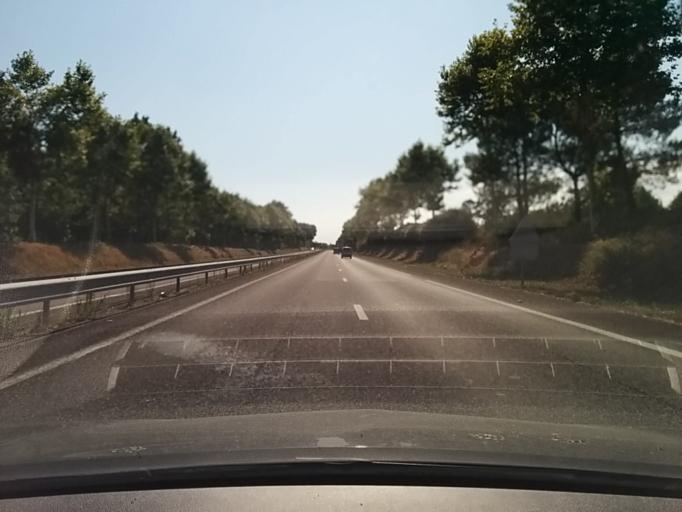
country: FR
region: Aquitaine
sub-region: Departement des Landes
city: Saint-Perdon
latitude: 43.8669
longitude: -0.6444
